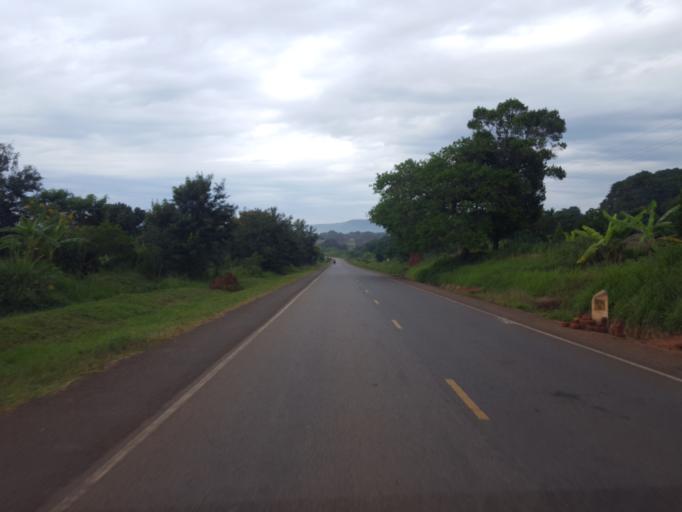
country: UG
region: Central Region
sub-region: Kiboga District
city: Kiboga
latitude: 0.9658
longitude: 31.7405
